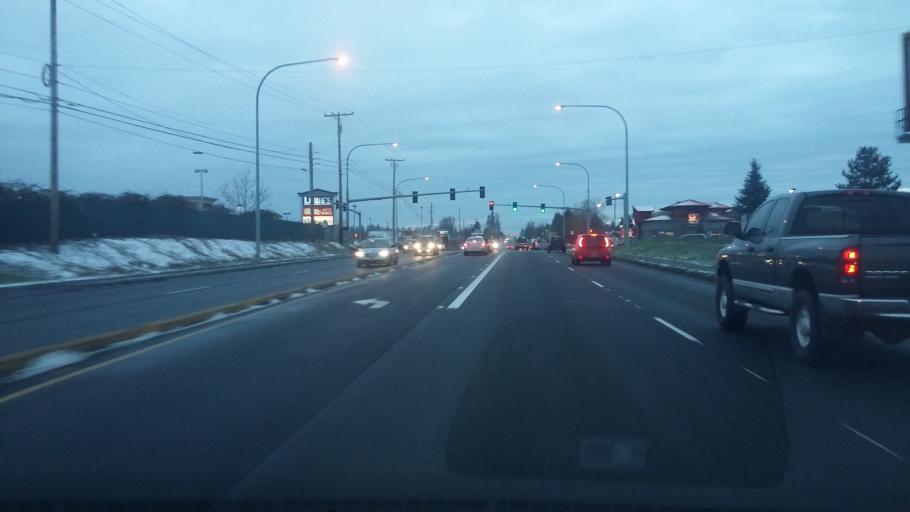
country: US
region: Washington
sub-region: Clark County
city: Orchards
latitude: 45.6736
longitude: -122.5526
